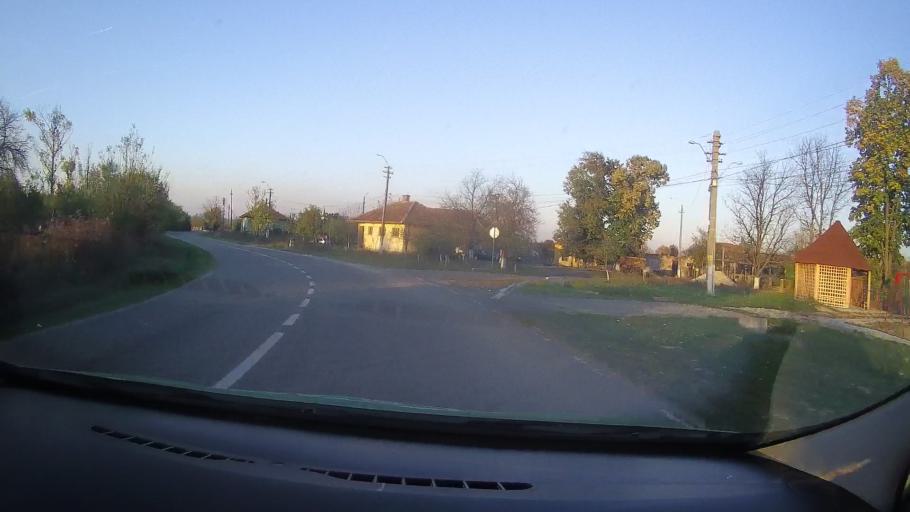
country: RO
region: Timis
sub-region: Comuna Traian Vuia
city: Traian Vuia
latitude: 45.7952
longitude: 22.0237
